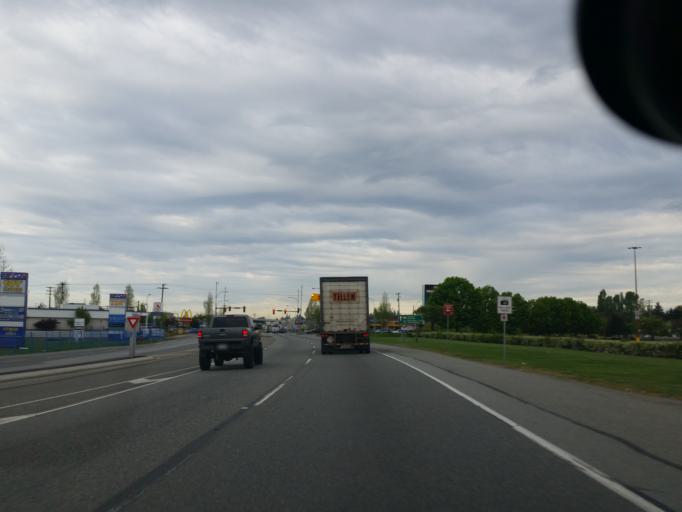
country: CA
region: British Columbia
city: Langley
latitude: 49.1131
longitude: -122.6730
